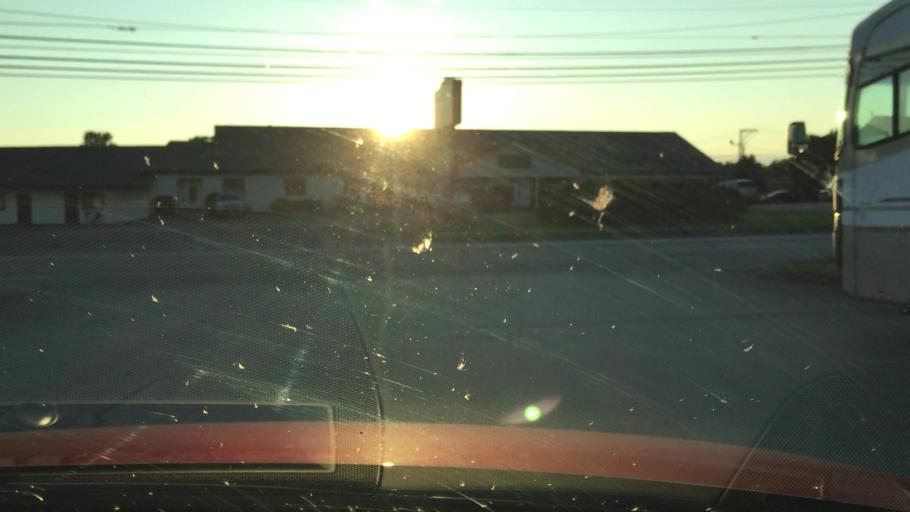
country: US
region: Maine
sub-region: Aroostook County
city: Houlton
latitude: 46.1441
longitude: -67.8401
